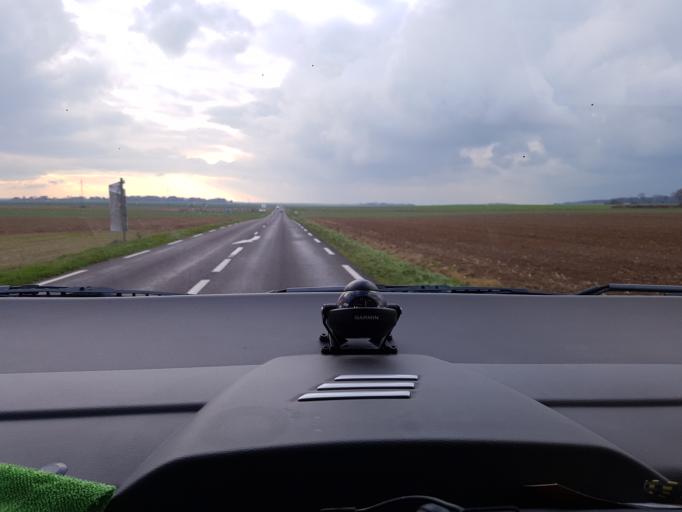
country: FR
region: Haute-Normandie
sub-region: Departement de la Seine-Maritime
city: Hautot-sur-Mer
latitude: 49.8904
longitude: 1.0277
